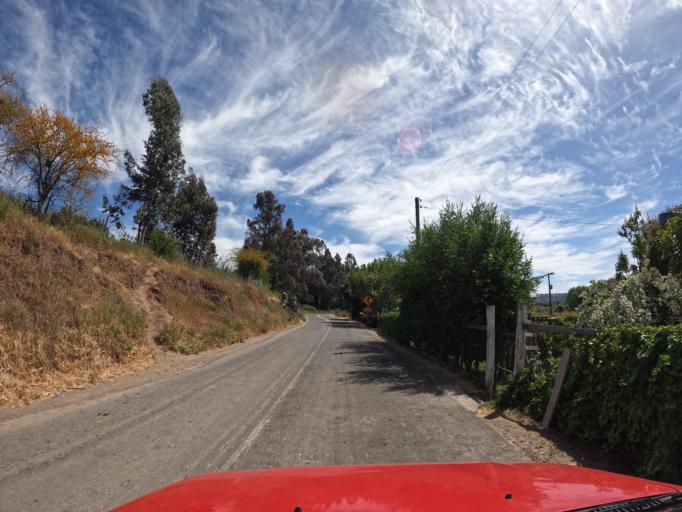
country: CL
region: Maule
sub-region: Provincia de Talca
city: Talca
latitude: -34.9897
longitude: -71.8453
